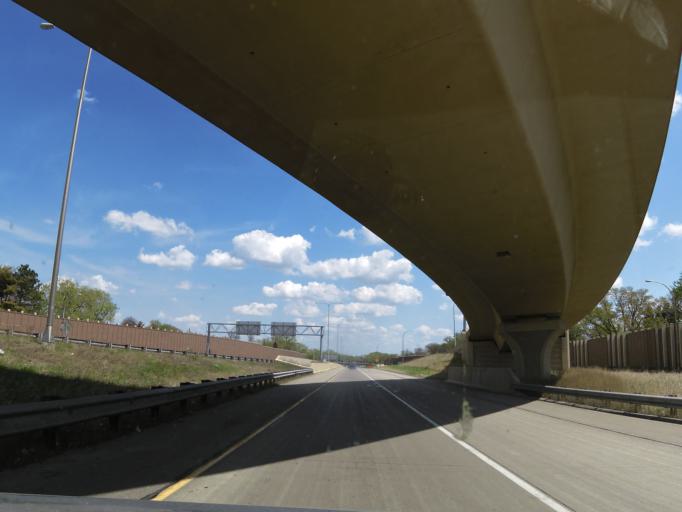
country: US
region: Minnesota
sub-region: Hennepin County
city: Richfield
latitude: 44.8906
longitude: -93.2745
